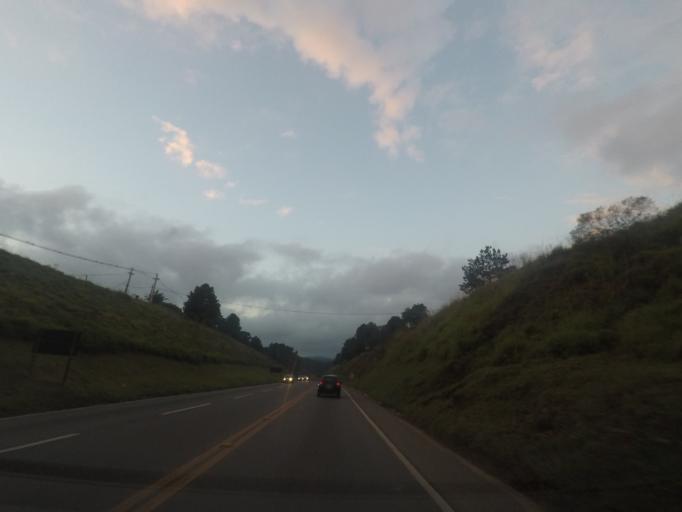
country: BR
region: Parana
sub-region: Curitiba
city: Curitiba
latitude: -25.4020
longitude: -49.3619
